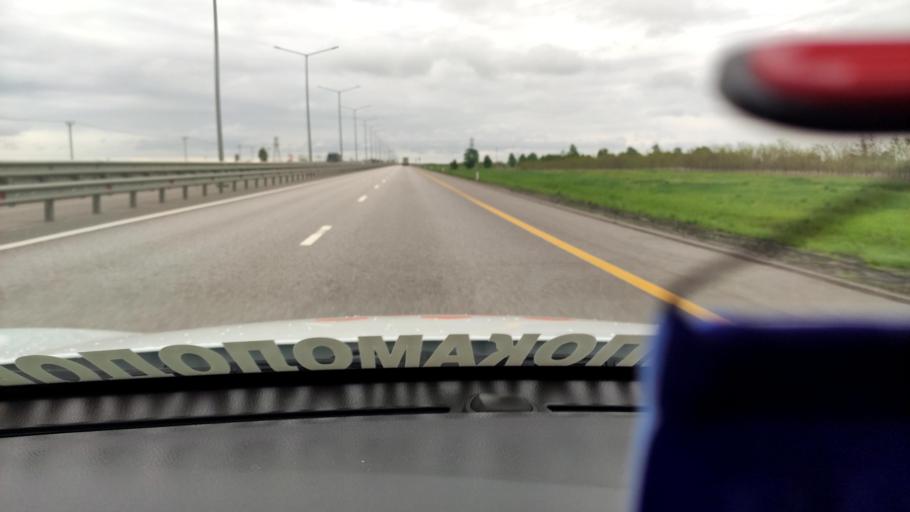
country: RU
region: Voronezj
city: Novaya Usman'
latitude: 51.5988
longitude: 39.3495
